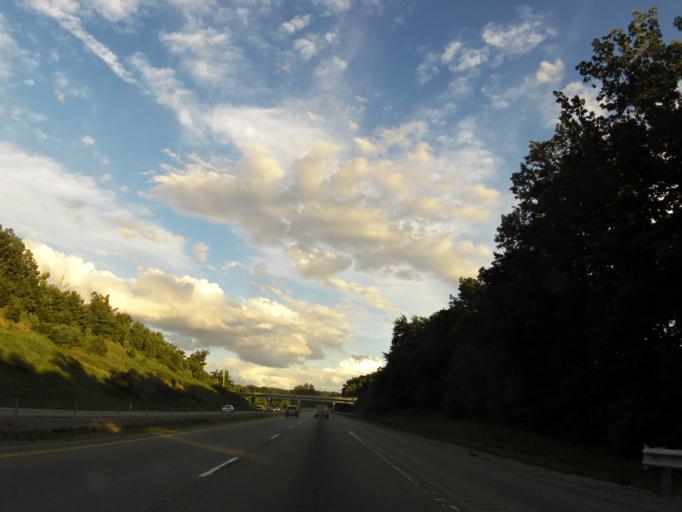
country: US
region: Tennessee
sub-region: Putnam County
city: Monterey
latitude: 36.1158
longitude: -85.2473
